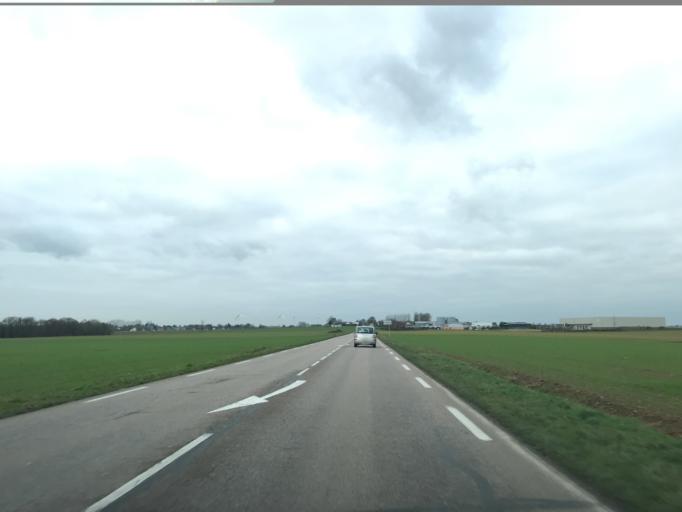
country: FR
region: Haute-Normandie
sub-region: Departement de l'Eure
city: Fleury-sur-Andelle
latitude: 49.3779
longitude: 1.3252
